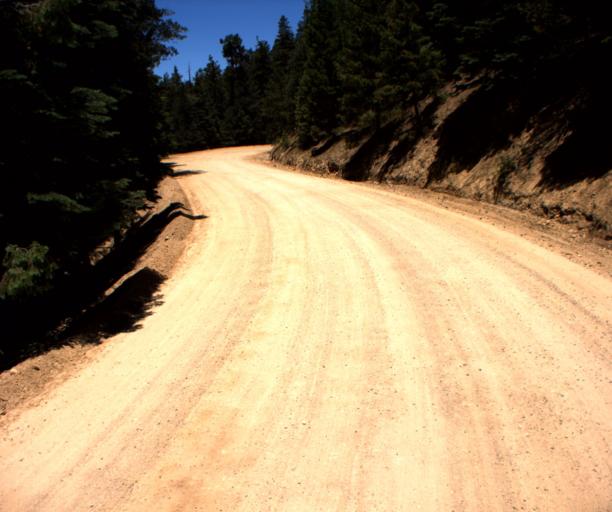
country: US
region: Arizona
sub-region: Graham County
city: Swift Trail Junction
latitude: 32.6623
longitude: -109.8674
